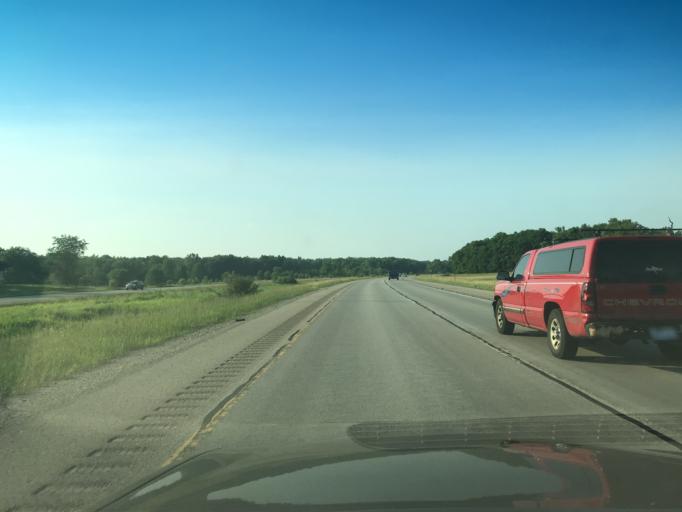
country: US
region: Michigan
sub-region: Ingham County
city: Holt
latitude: 42.6403
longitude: -84.4786
